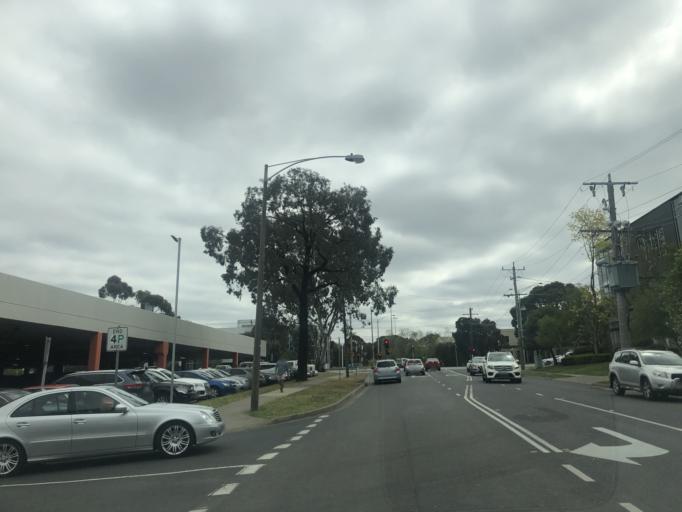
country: AU
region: Victoria
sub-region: Monash
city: Notting Hill
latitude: -37.9047
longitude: 145.1636
